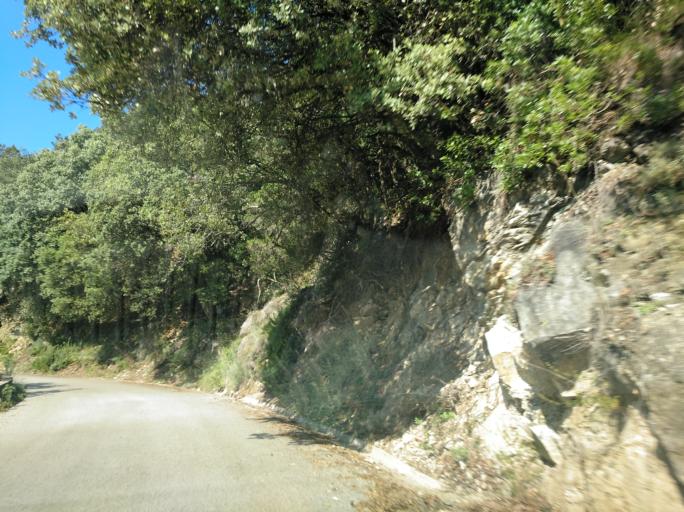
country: ES
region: Catalonia
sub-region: Provincia de Girona
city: Susqueda
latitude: 41.9849
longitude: 2.5279
